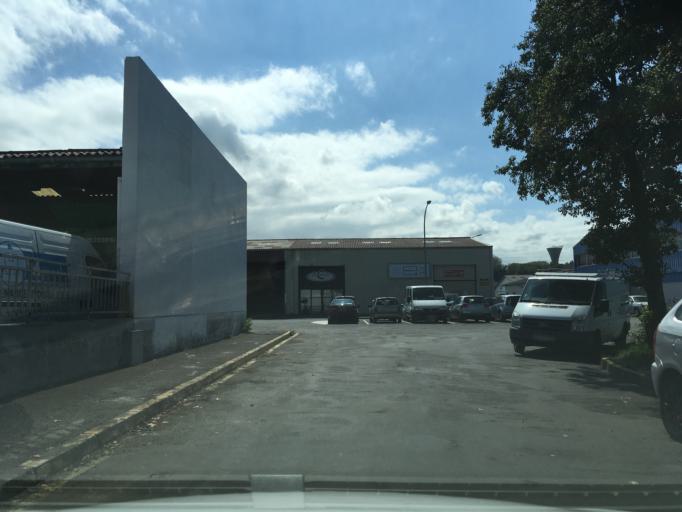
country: FR
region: Aquitaine
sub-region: Departement des Pyrenees-Atlantiques
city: Bayonne
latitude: 43.4899
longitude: -1.4541
